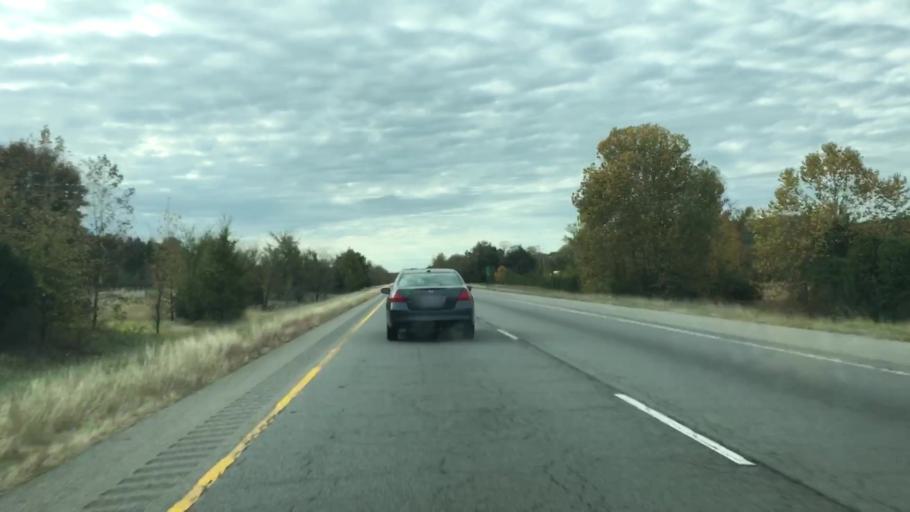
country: US
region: Arkansas
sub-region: Faulkner County
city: Conway
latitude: 35.1197
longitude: -92.4686
